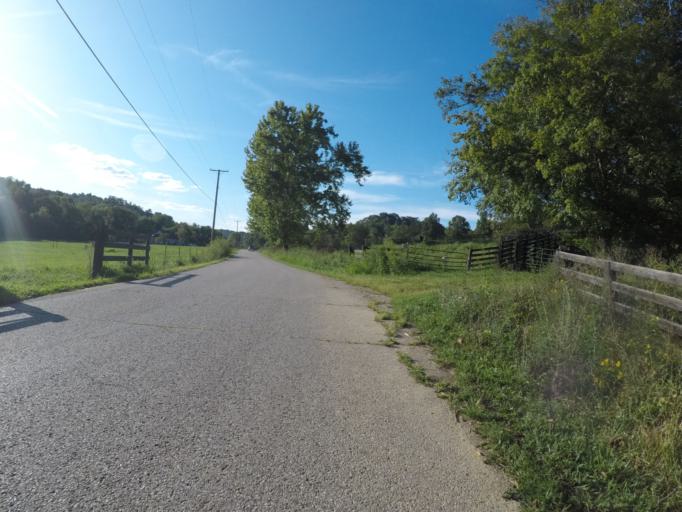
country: US
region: West Virginia
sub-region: Cabell County
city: Huntington
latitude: 38.5068
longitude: -82.4906
